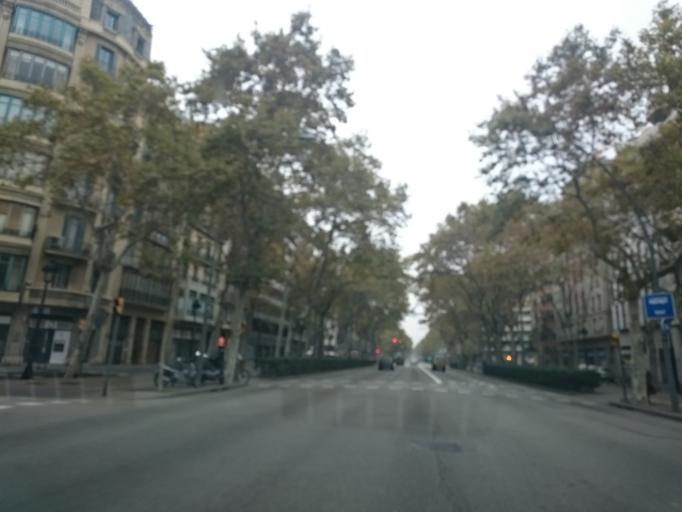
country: ES
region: Catalonia
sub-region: Provincia de Barcelona
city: Barcelona
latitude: 41.3812
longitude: 2.1573
